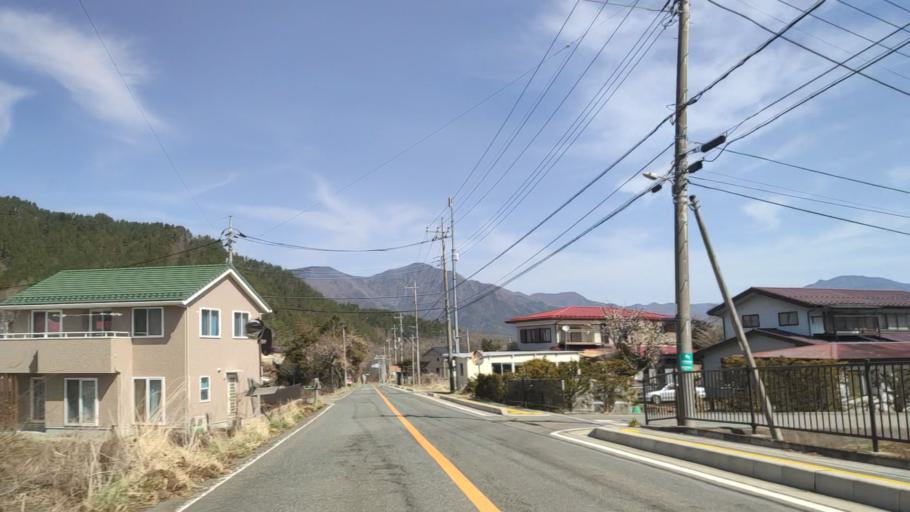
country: JP
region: Yamanashi
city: Fujikawaguchiko
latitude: 35.4884
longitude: 138.7274
